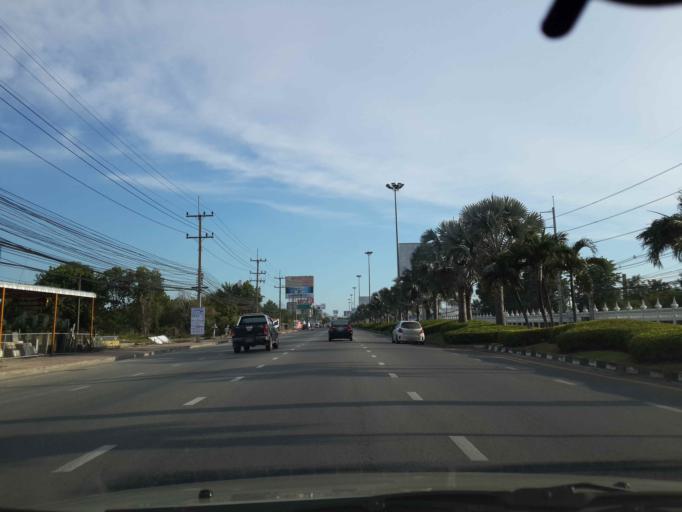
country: TH
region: Chon Buri
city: Bang Lamung
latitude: 12.9942
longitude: 100.9271
